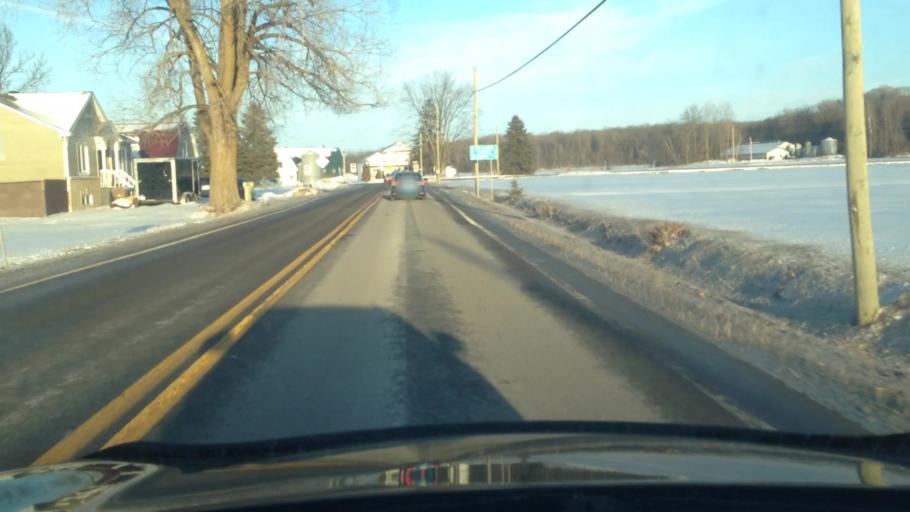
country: CA
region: Quebec
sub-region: Lanaudiere
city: Sainte-Julienne
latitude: 45.9133
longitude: -73.7383
